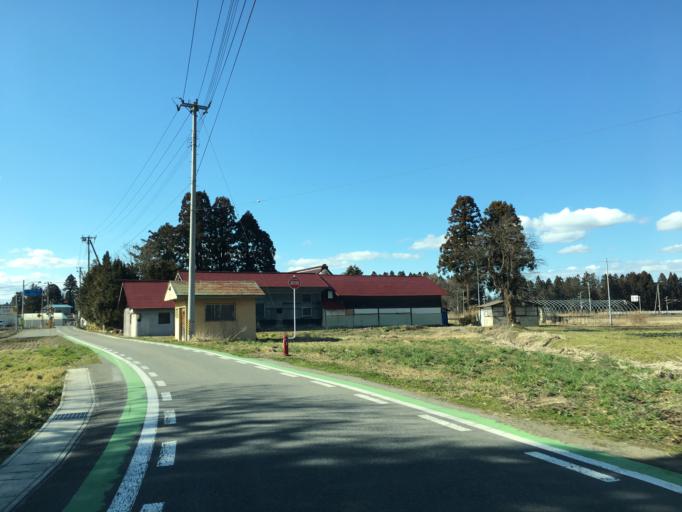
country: JP
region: Yamagata
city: Yonezawa
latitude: 37.9443
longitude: 140.1388
